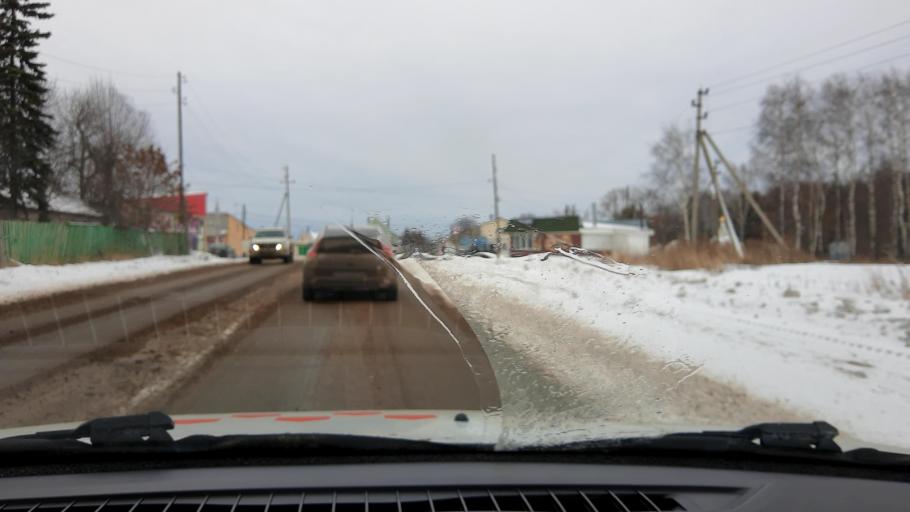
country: RU
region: Nizjnij Novgorod
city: Gorodets
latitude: 56.6451
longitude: 43.5017
